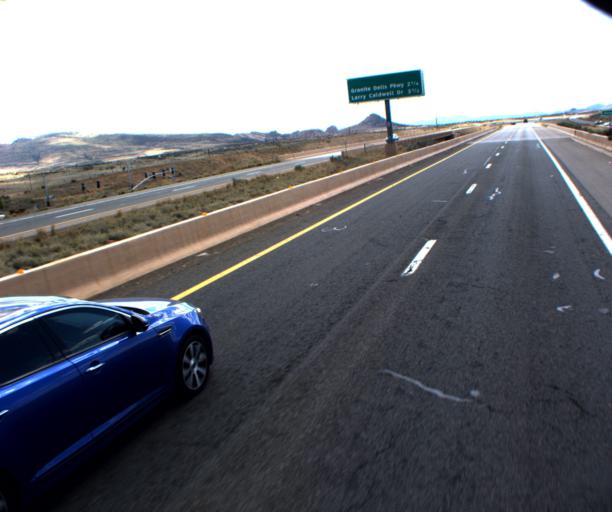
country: US
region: Arizona
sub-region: Yavapai County
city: Prescott Valley
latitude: 34.6323
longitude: -112.3539
